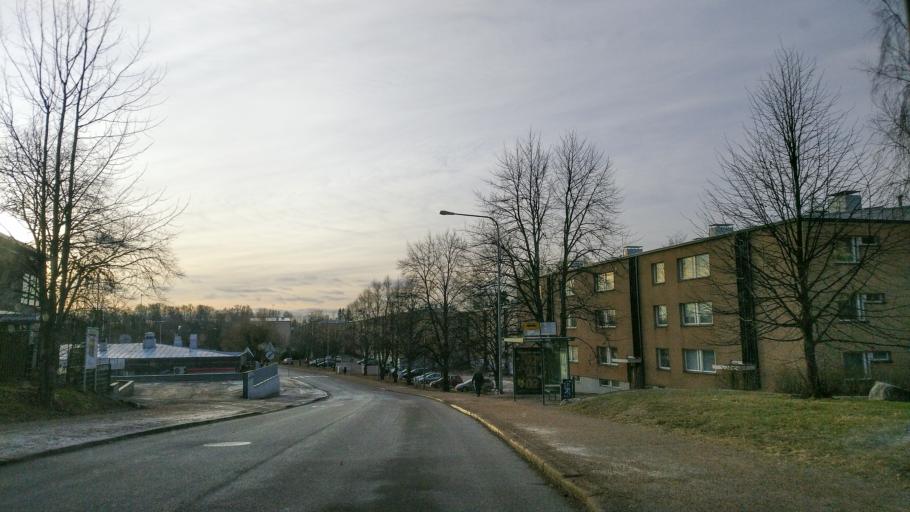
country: FI
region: Uusimaa
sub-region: Helsinki
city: Vantaa
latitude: 60.1977
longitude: 25.0552
